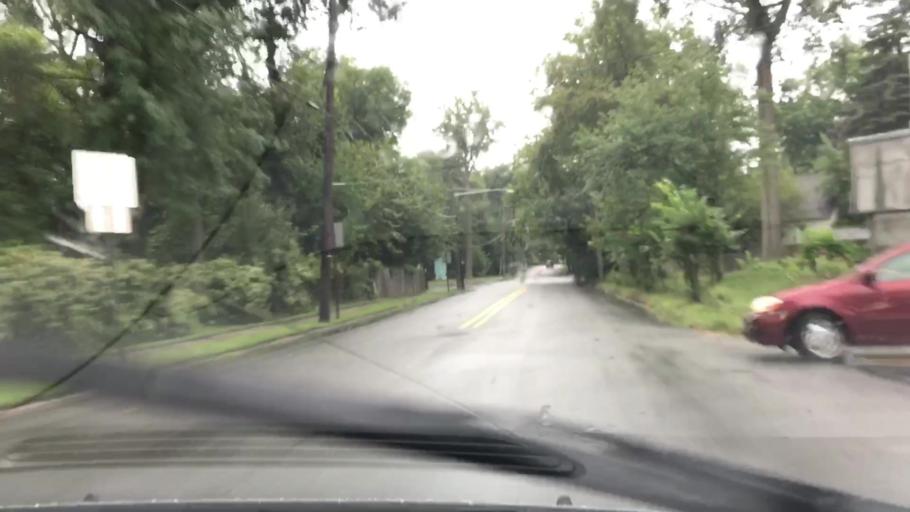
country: US
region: New Jersey
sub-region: Bergen County
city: Bergenfield
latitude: 40.9099
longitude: -73.9903
